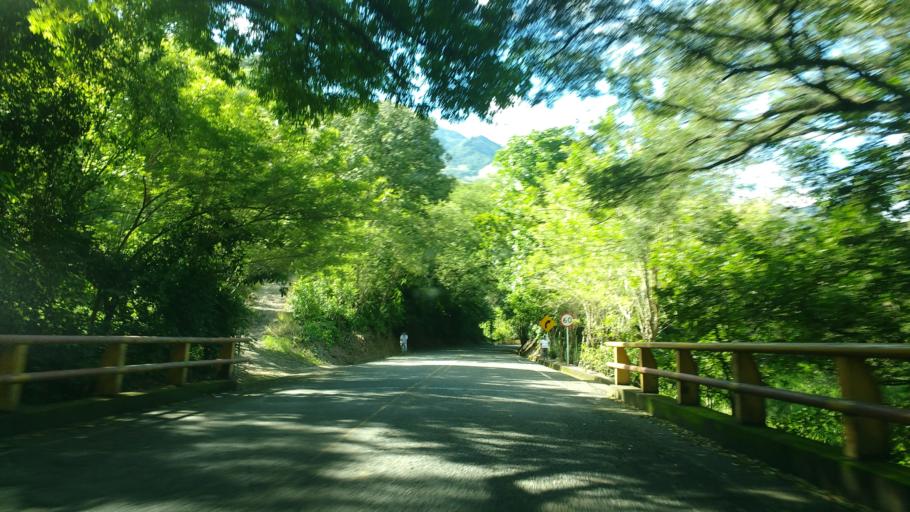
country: CO
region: Antioquia
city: Concordia
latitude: 6.0371
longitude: -75.8582
